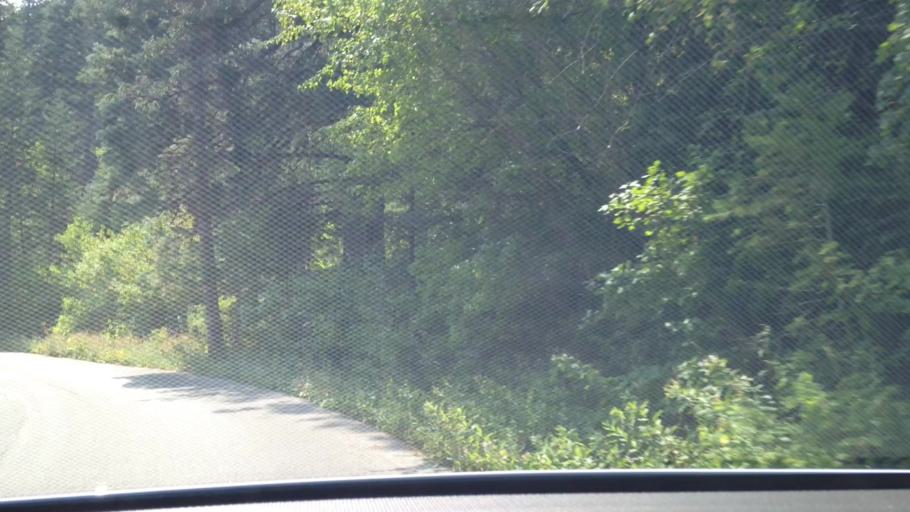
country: US
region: Utah
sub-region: Summit County
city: Summit Park
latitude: 40.7004
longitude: -111.6868
